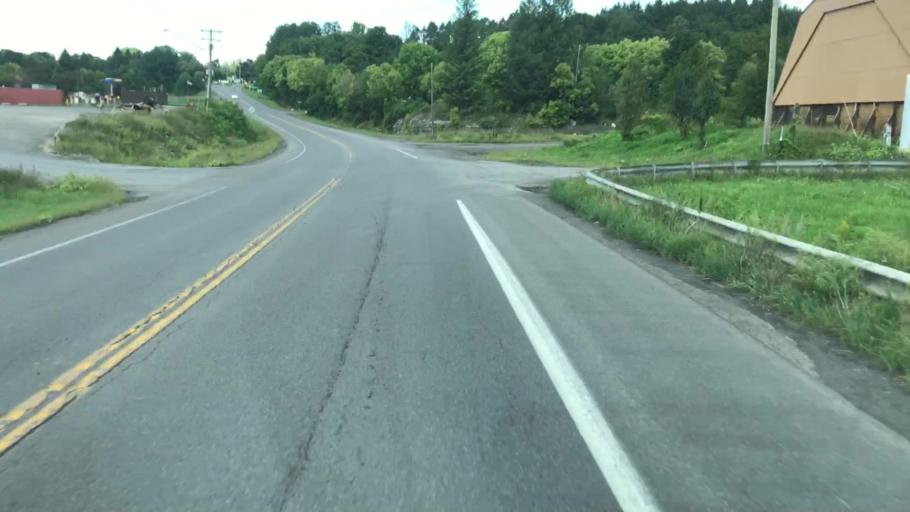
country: US
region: New York
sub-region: Onondaga County
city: Marcellus
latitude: 42.9779
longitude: -76.3312
